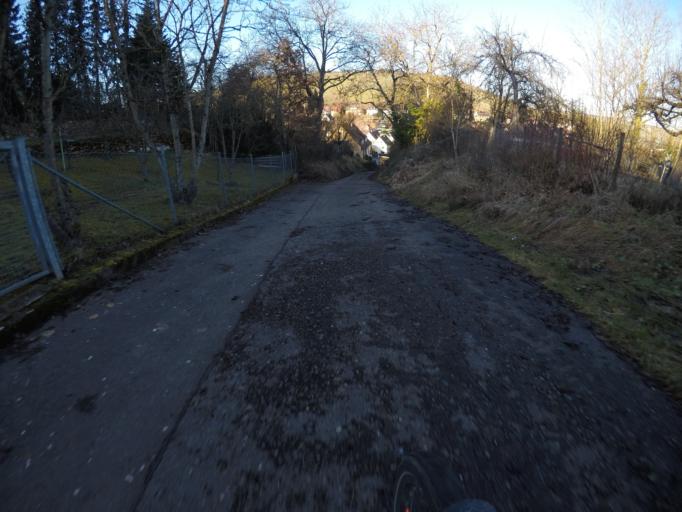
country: DE
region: Baden-Wuerttemberg
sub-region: Regierungsbezirk Stuttgart
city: Ostfildern
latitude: 48.7548
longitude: 9.2483
